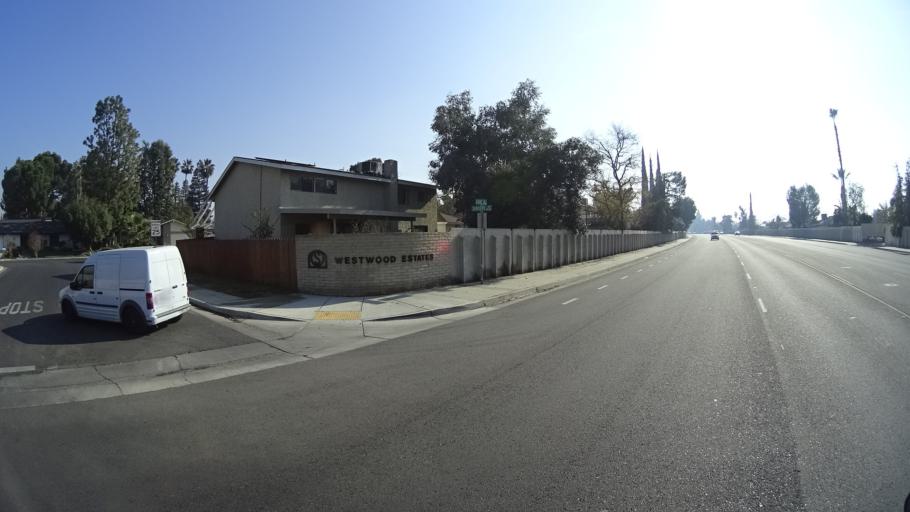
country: US
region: California
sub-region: Kern County
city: Greenacres
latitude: 35.3444
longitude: -119.0742
